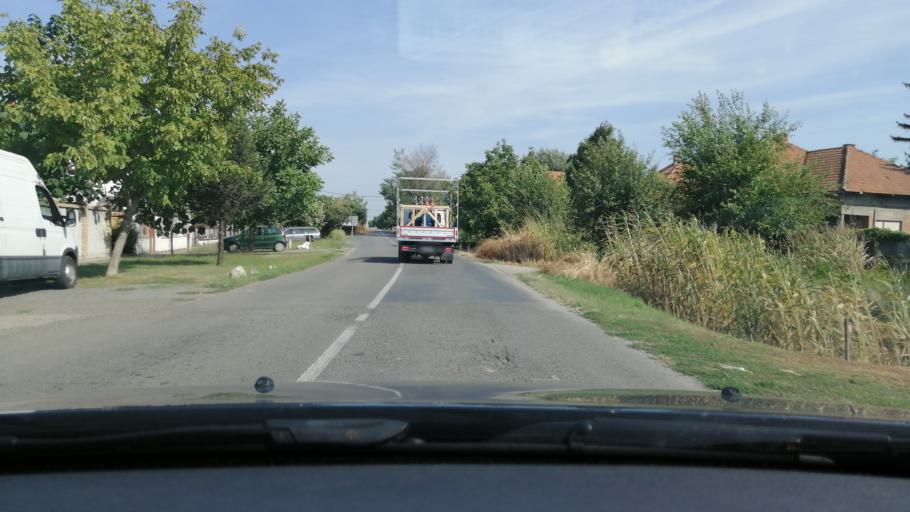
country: RS
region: Autonomna Pokrajina Vojvodina
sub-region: Juznobanatski Okrug
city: Kovacica
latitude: 45.1187
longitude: 20.6170
